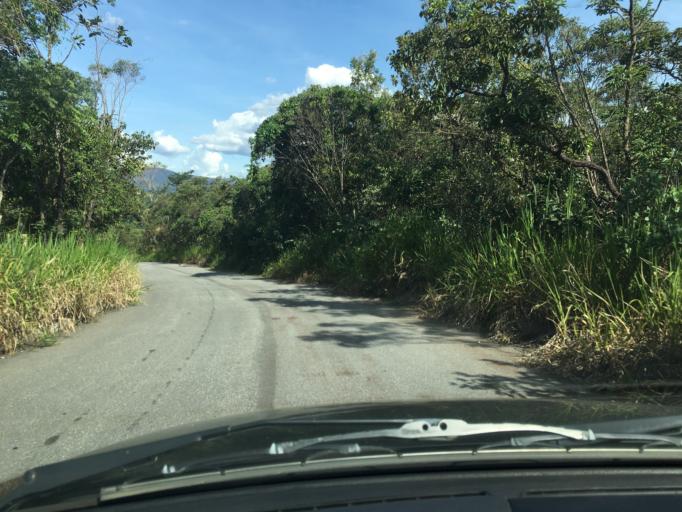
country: BR
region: Minas Gerais
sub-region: Ibirite
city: Ibirite
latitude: -20.1319
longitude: -44.0700
